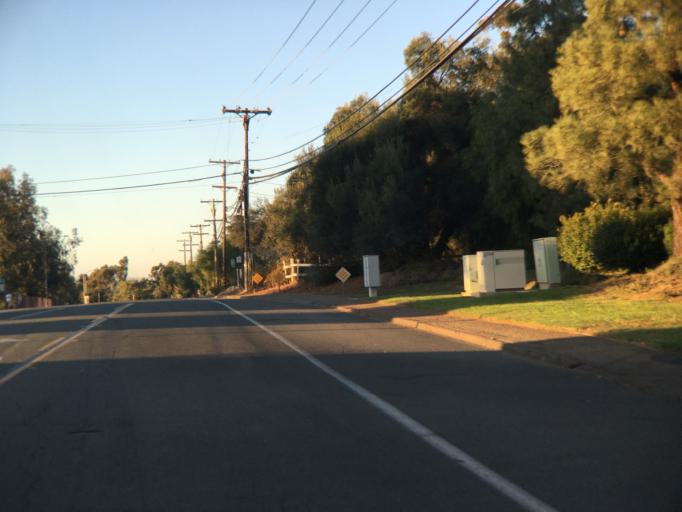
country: US
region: California
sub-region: San Diego County
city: Alpine
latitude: 32.8179
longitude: -116.7760
